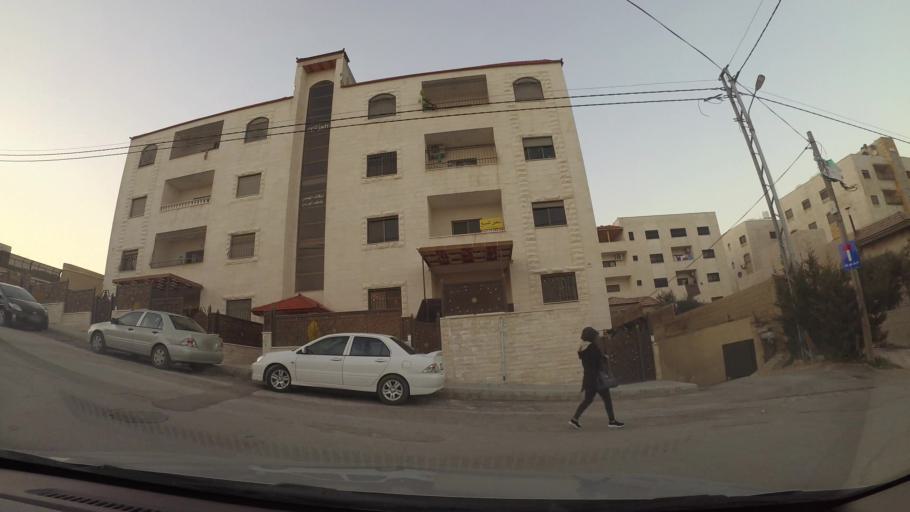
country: JO
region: Amman
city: Al Quwaysimah
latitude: 31.8957
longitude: 35.9278
